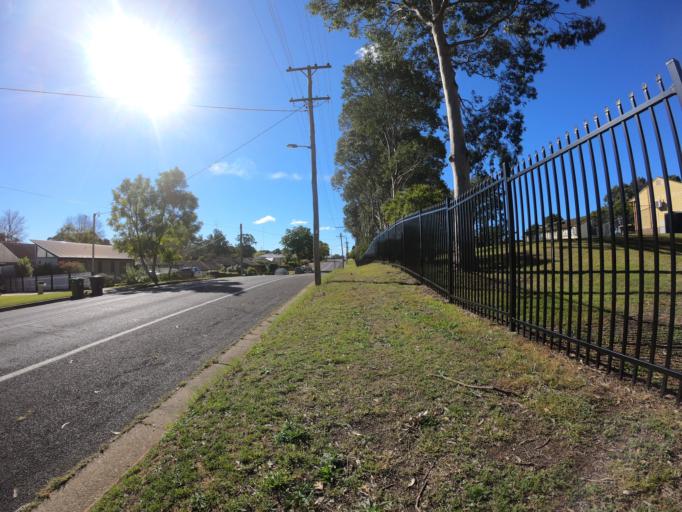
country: AU
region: New South Wales
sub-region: Hawkesbury
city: South Windsor
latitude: -33.6184
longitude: 150.8030
